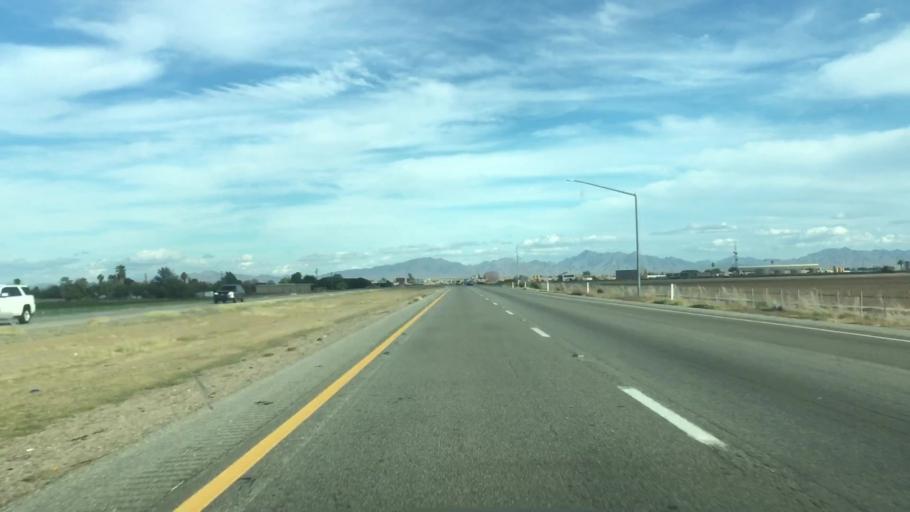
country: US
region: California
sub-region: Riverside County
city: Blythe
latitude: 33.6065
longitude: -114.6536
